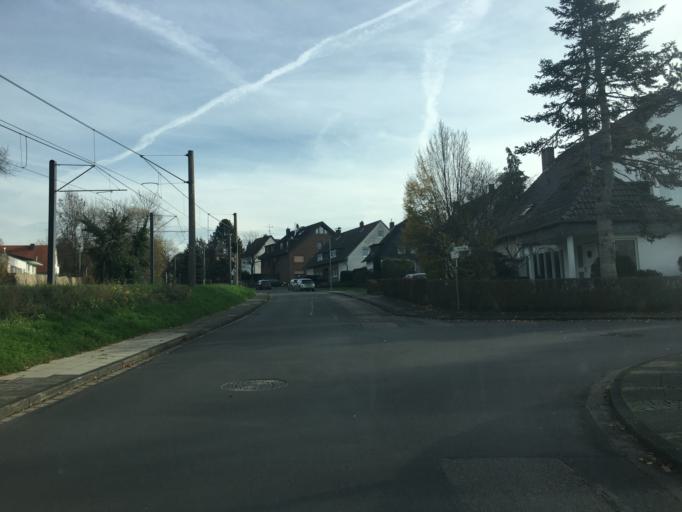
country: DE
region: North Rhine-Westphalia
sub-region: Regierungsbezirk Koln
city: Bergisch Gladbach
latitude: 50.9614
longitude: 7.1513
